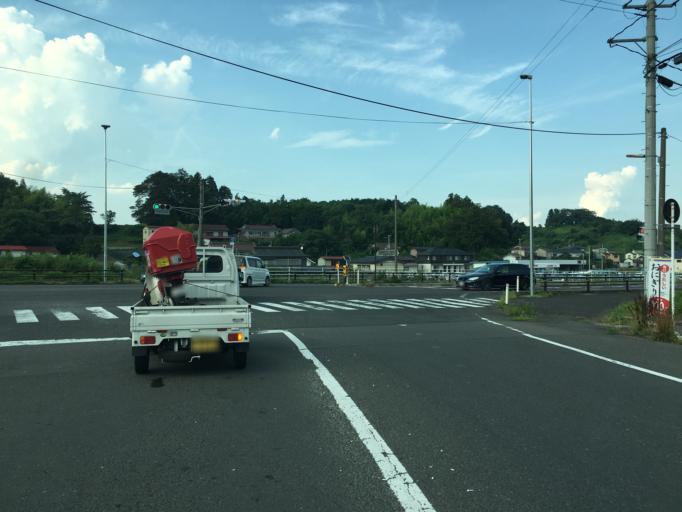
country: JP
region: Fukushima
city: Nihommatsu
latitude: 37.5839
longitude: 140.4402
